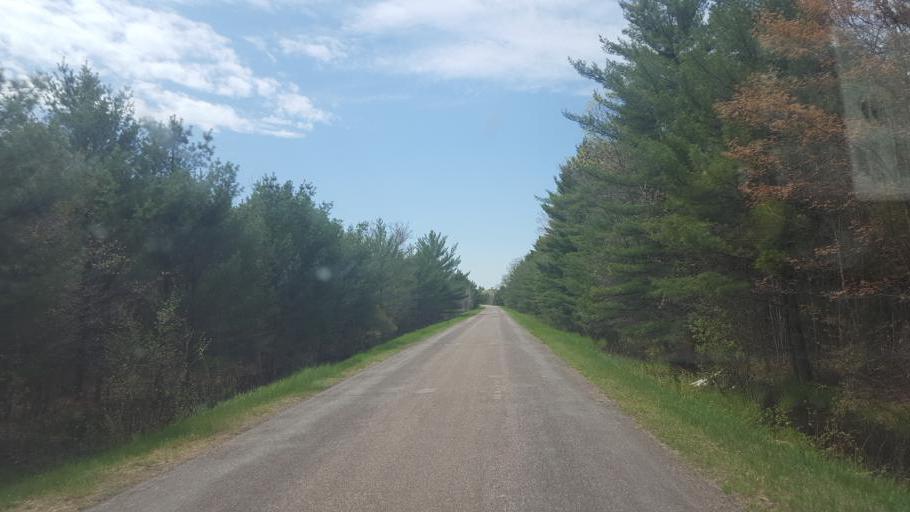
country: US
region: Wisconsin
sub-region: Clark County
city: Neillsville
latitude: 44.2861
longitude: -90.4966
